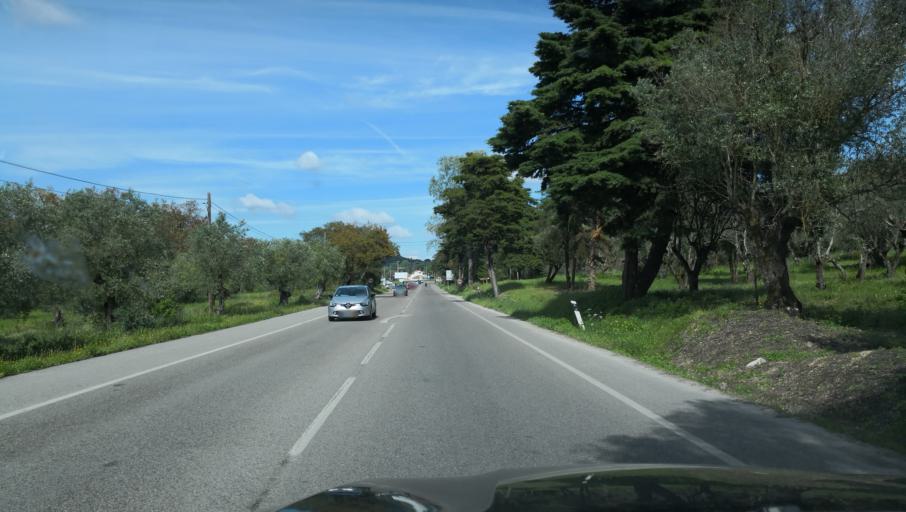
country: PT
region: Setubal
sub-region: Palmela
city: Quinta do Anjo
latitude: 38.5230
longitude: -9.0039
